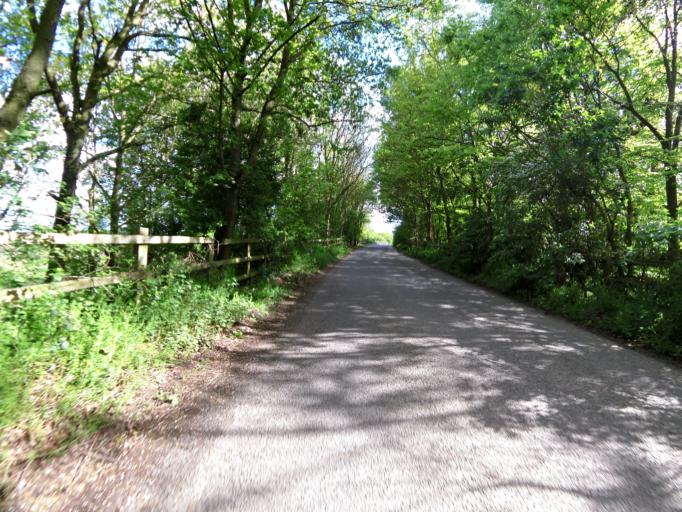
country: GB
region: England
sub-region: Suffolk
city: Woolpit
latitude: 52.2305
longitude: 0.8583
